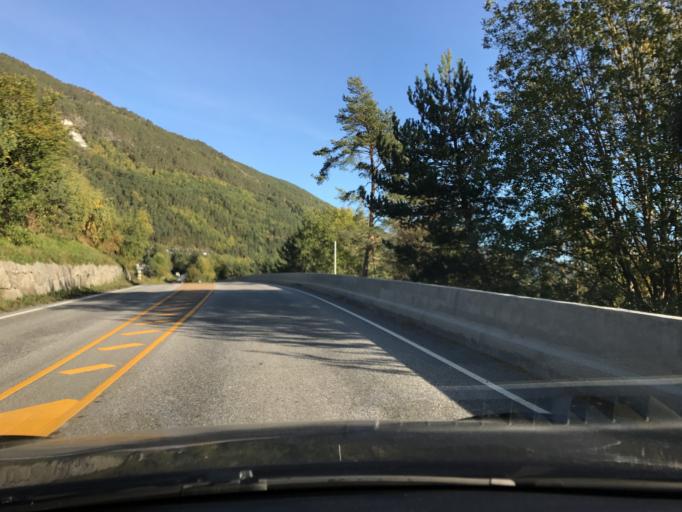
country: NO
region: Sogn og Fjordane
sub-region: Sogndal
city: Sogndalsfjora
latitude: 61.2112
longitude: 7.1290
